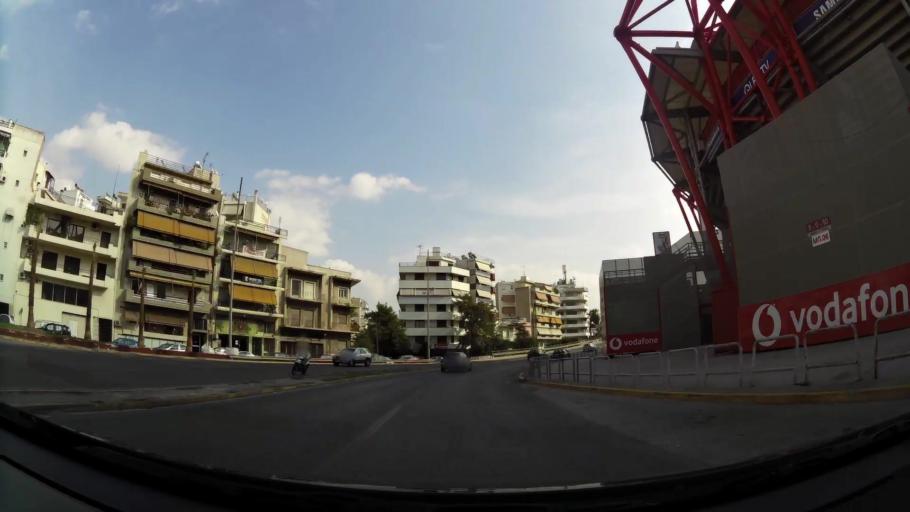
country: GR
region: Attica
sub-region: Nomarchia Athinas
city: Moskhaton
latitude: 37.9475
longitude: 23.6649
